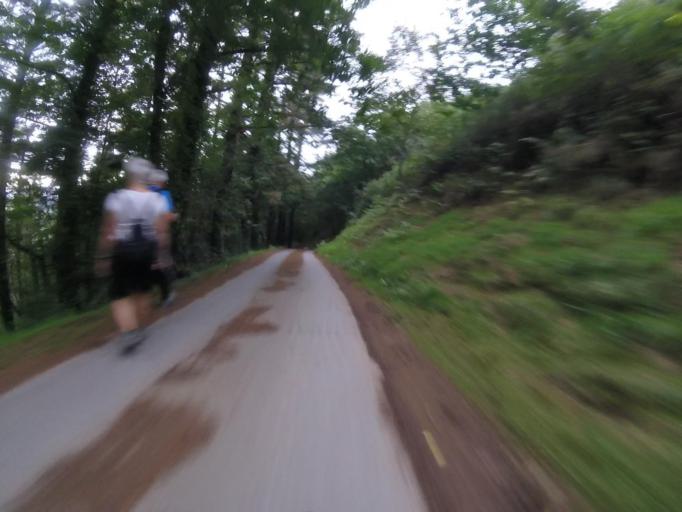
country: ES
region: Basque Country
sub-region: Provincia de Guipuzcoa
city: Errenteria
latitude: 43.2711
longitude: -1.8330
